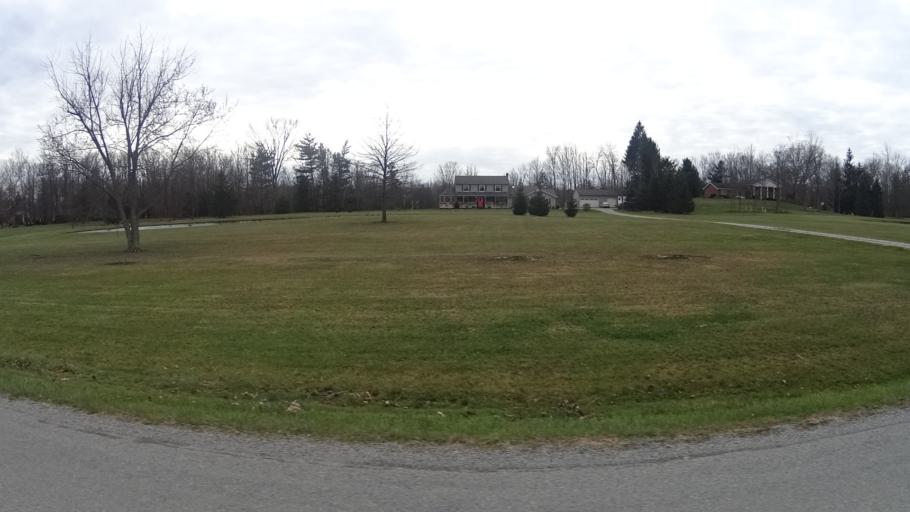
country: US
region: Ohio
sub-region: Lorain County
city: Wellington
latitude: 41.1901
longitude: -82.2468
